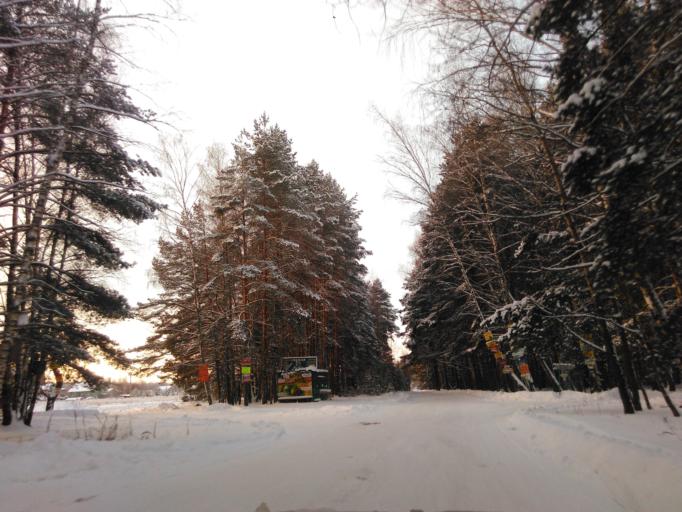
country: RU
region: Tverskaya
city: Konakovo
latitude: 56.6553
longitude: 36.6588
